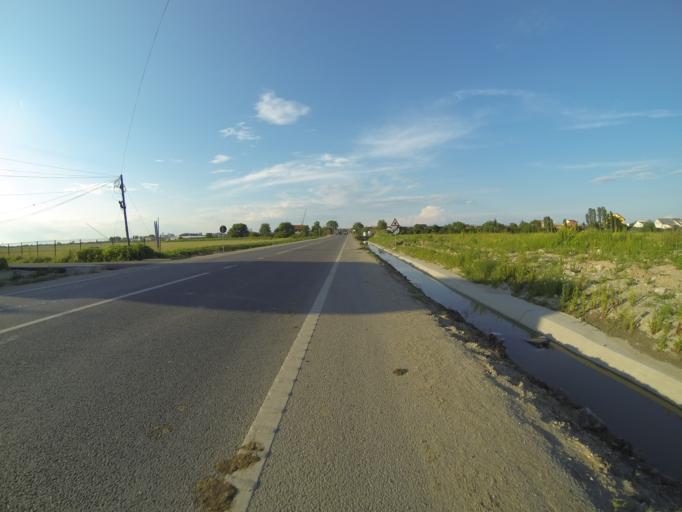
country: RO
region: Dolj
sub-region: Municipiul Craiova
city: Popoveni
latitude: 44.2818
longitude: 23.7967
